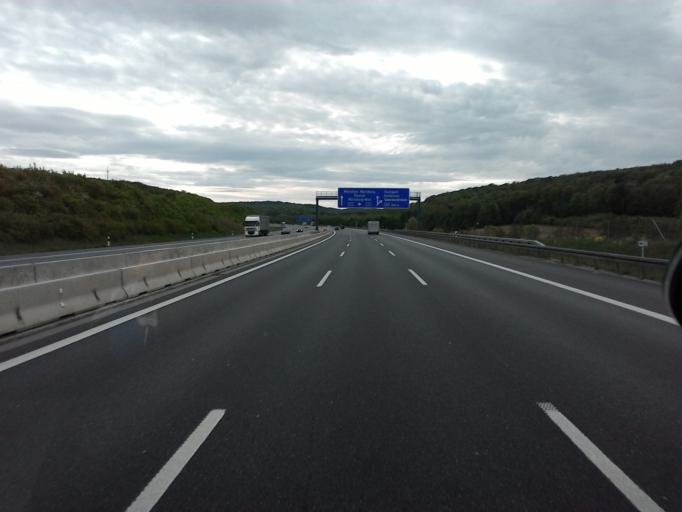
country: DE
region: Bavaria
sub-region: Regierungsbezirk Unterfranken
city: Waldbrunn
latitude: 49.7503
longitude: 9.7957
